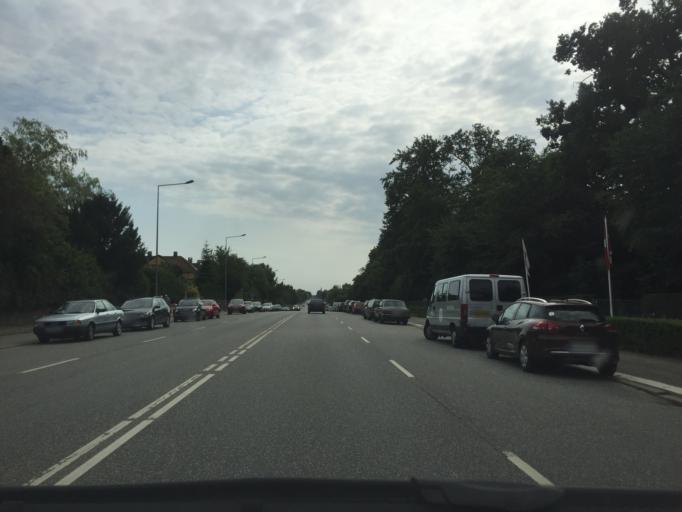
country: DK
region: Capital Region
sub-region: Gentofte Kommune
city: Charlottenlund
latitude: 55.7559
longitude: 12.5581
